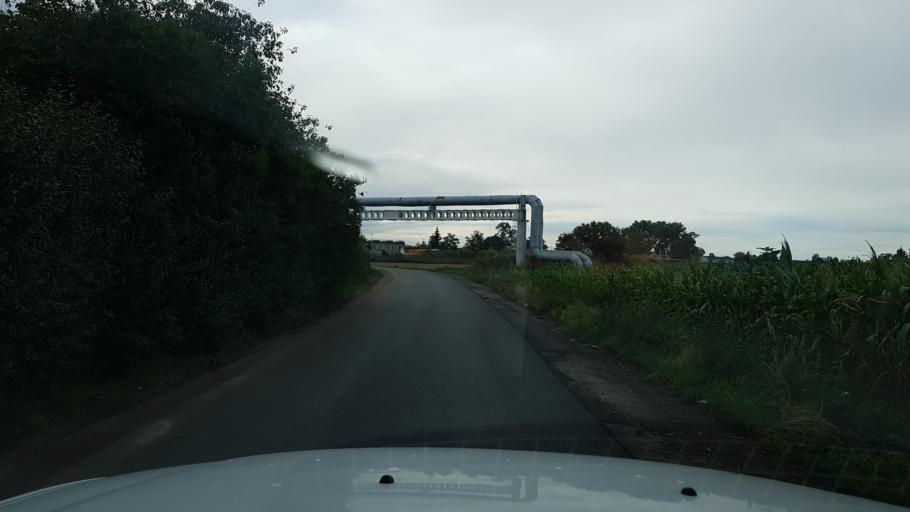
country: PL
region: West Pomeranian Voivodeship
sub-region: Powiat stargardzki
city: Stargard Szczecinski
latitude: 53.3213
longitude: 15.0276
